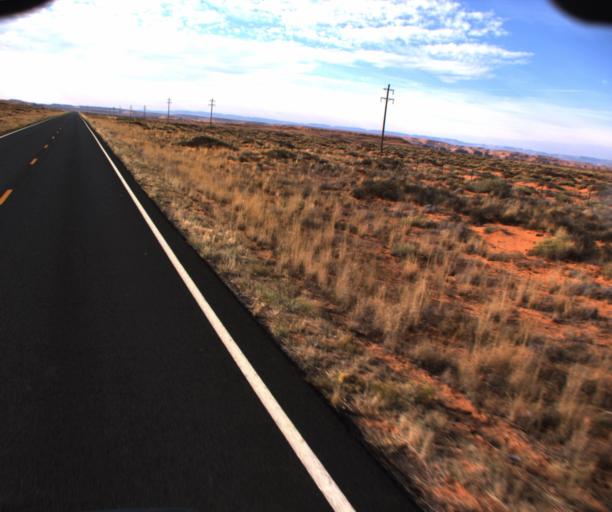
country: US
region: Arizona
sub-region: Apache County
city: Many Farms
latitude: 36.8361
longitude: -109.6428
